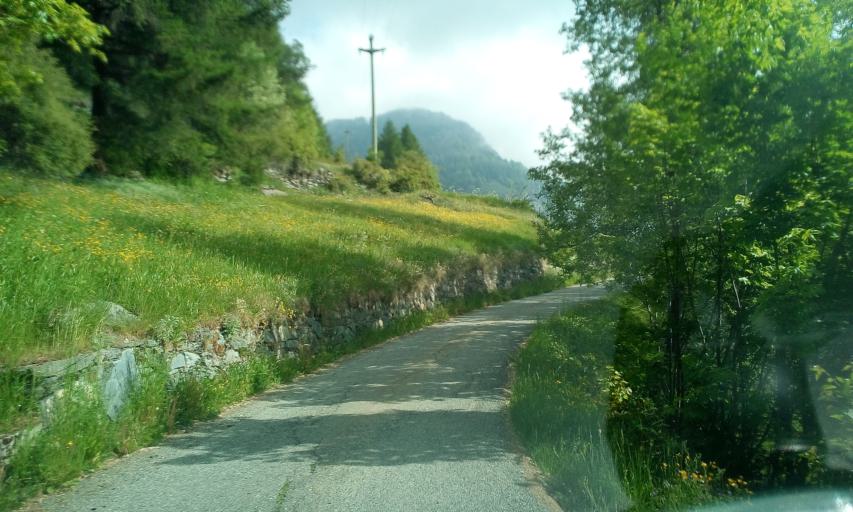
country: IT
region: Aosta Valley
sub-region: Valle d'Aosta
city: Torgnon
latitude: 45.8158
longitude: 7.5782
